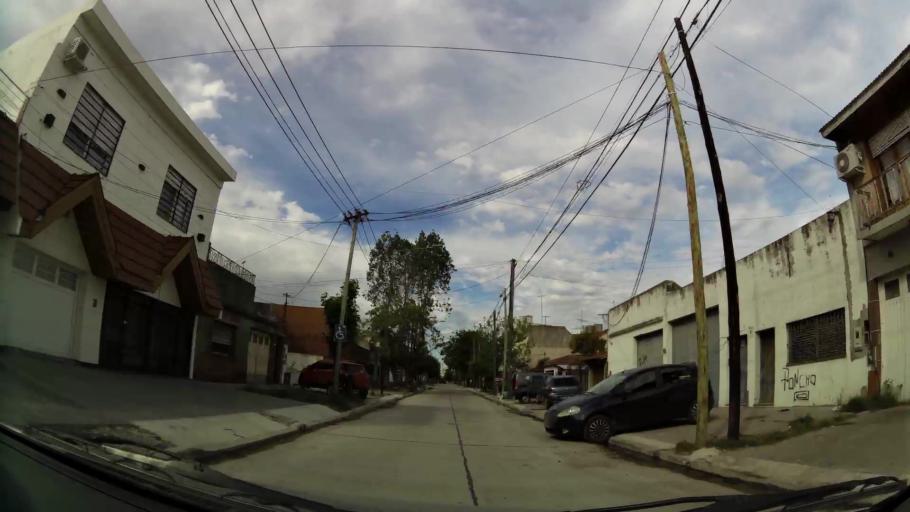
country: AR
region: Buenos Aires
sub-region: Partido de Lanus
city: Lanus
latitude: -34.6951
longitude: -58.3764
